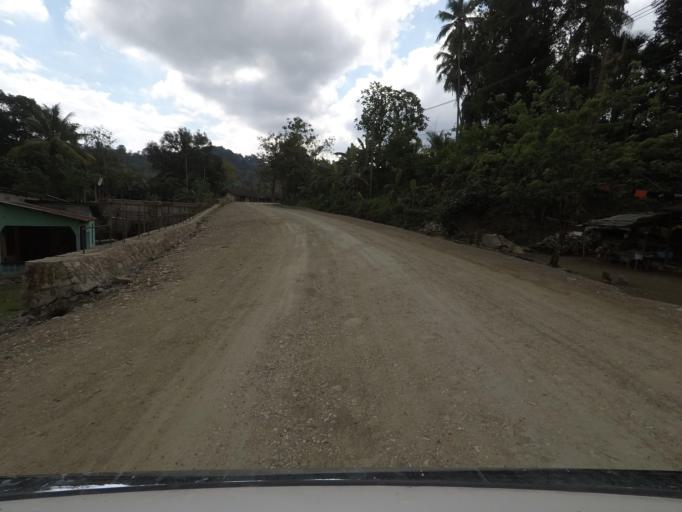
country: TL
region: Viqueque
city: Viqueque
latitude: -8.8327
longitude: 126.3730
